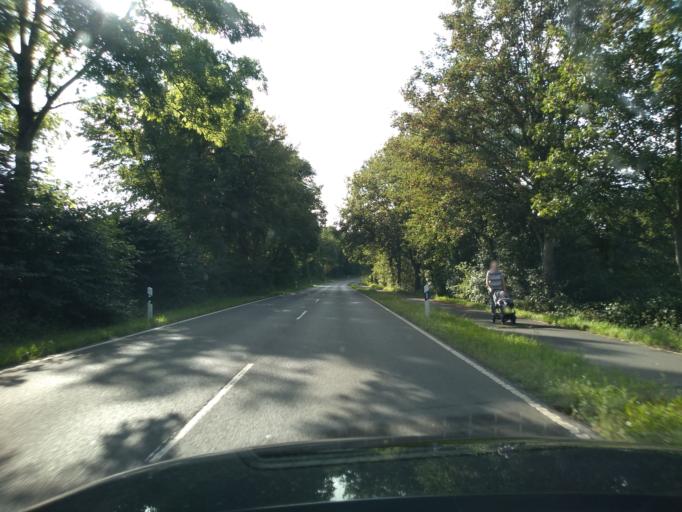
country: DE
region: North Rhine-Westphalia
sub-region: Regierungsbezirk Koln
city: Much
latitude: 50.8495
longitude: 7.3874
